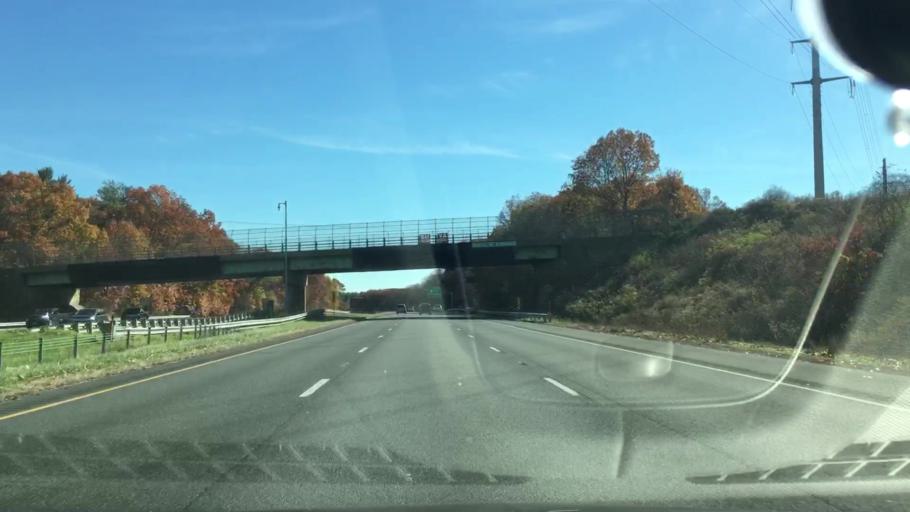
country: US
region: Massachusetts
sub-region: Hampden County
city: Chicopee
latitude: 42.1434
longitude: -72.6398
